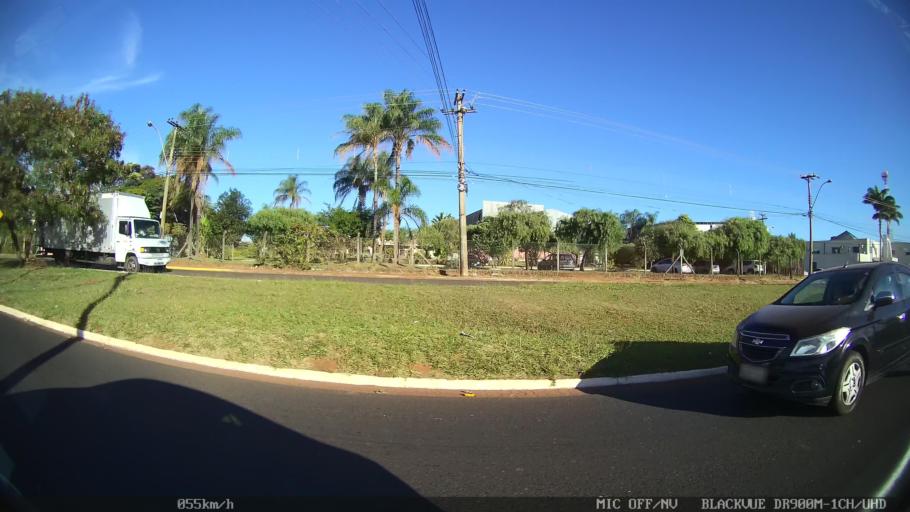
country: BR
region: Sao Paulo
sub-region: Americo Brasiliense
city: Americo Brasiliense
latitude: -21.7440
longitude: -48.1260
